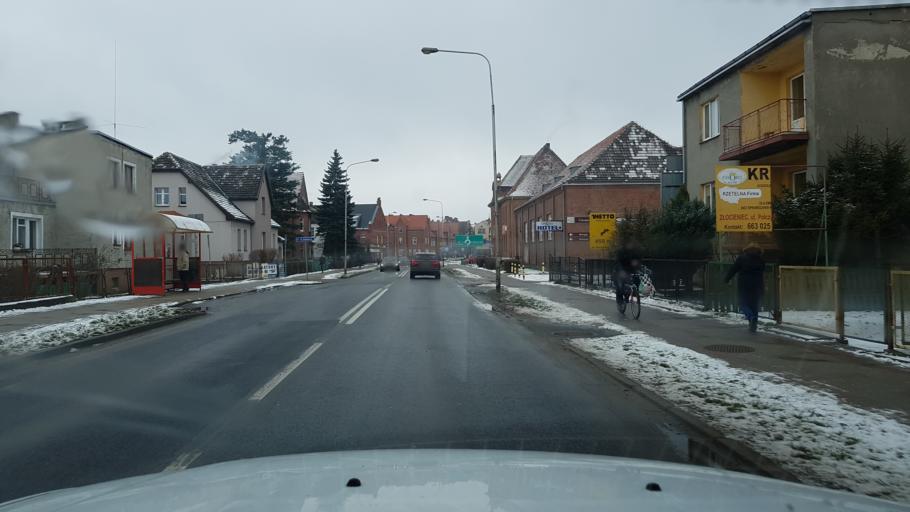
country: PL
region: West Pomeranian Voivodeship
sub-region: Powiat drawski
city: Zlocieniec
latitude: 53.5339
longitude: 16.0185
